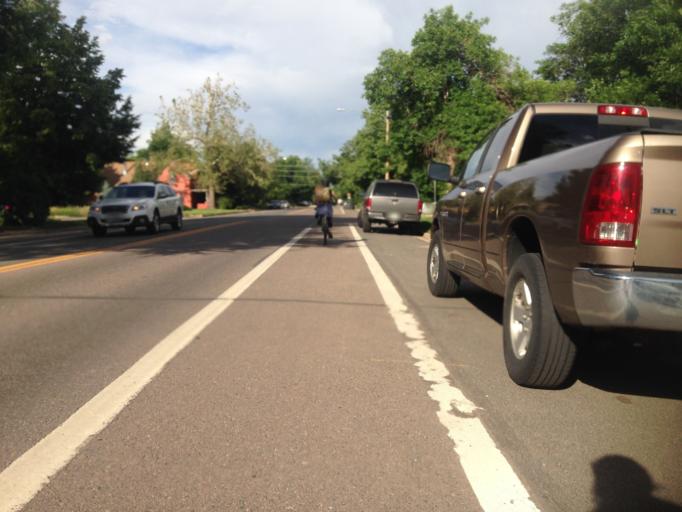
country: US
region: Colorado
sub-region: Boulder County
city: Boulder
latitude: 40.0224
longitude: -105.2682
